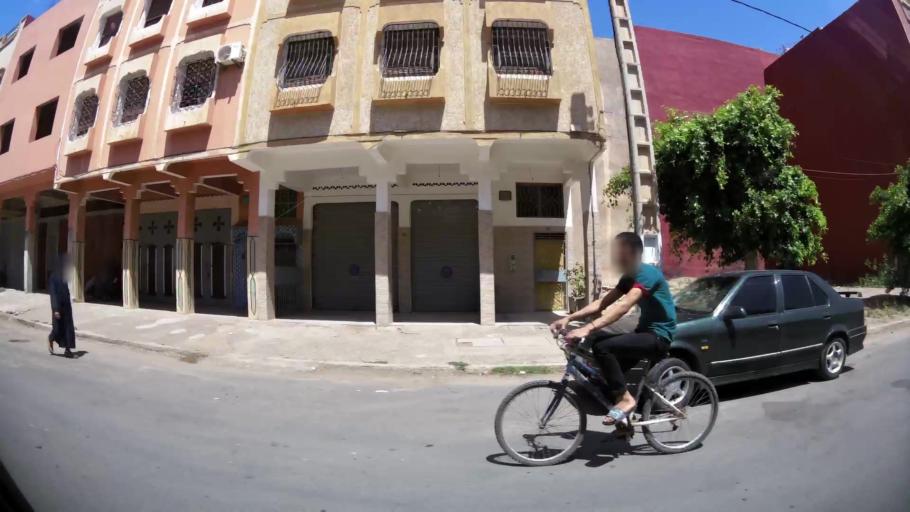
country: MA
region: Souss-Massa-Draa
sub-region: Inezgane-Ait Mellou
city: Inezgane
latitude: 30.3381
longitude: -9.5024
